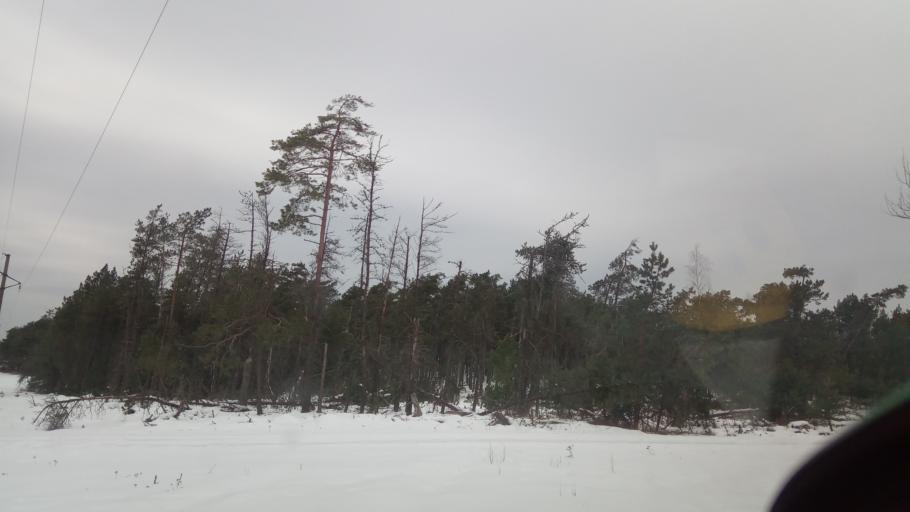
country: LT
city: Neringa
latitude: 55.4192
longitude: 21.0934
